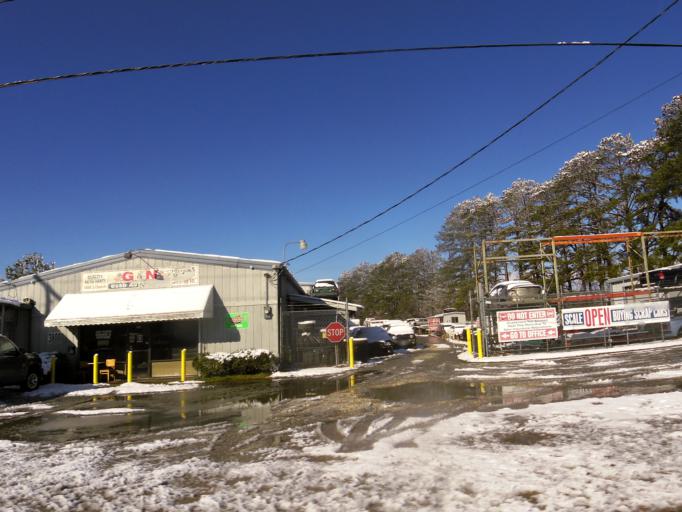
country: US
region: North Carolina
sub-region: Nash County
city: Sharpsburg
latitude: 35.8995
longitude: -77.8151
